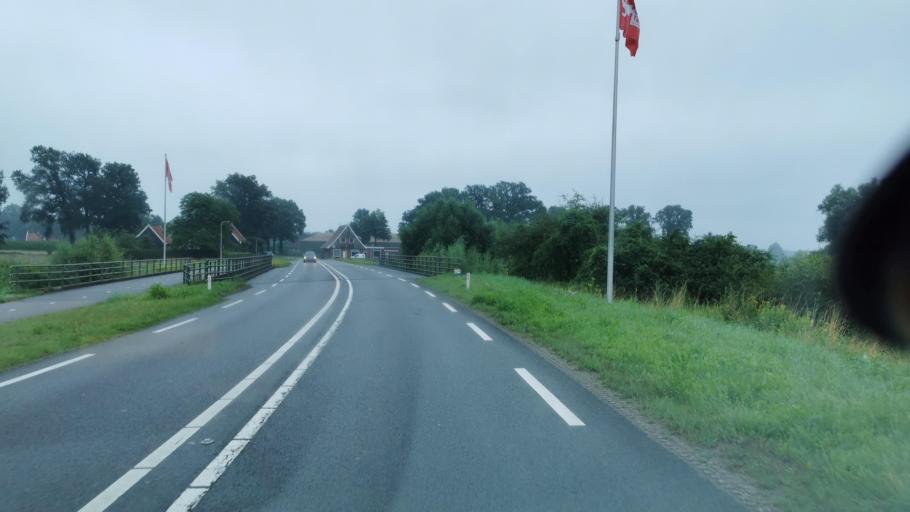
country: NL
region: Overijssel
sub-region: Gemeente Losser
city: Losser
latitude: 52.2507
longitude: 7.0169
